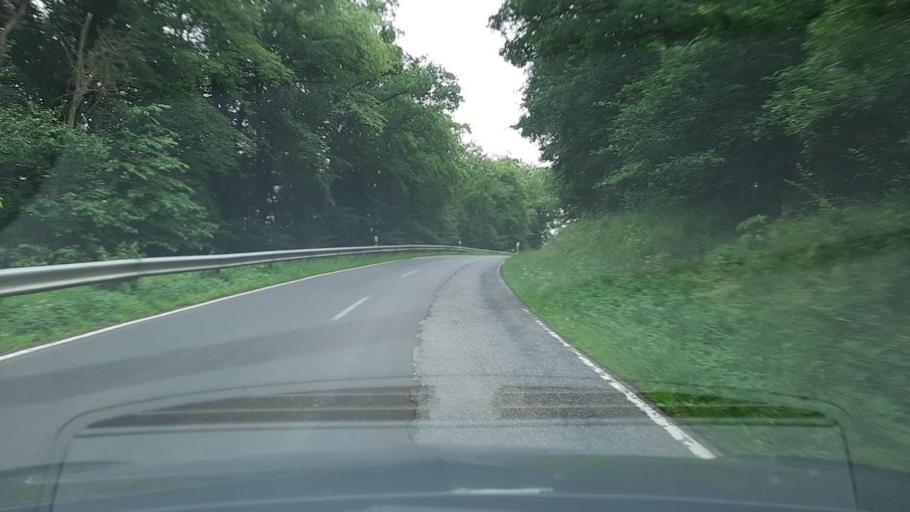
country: DE
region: Rheinland-Pfalz
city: Beltheim
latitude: 50.0921
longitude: 7.4523
